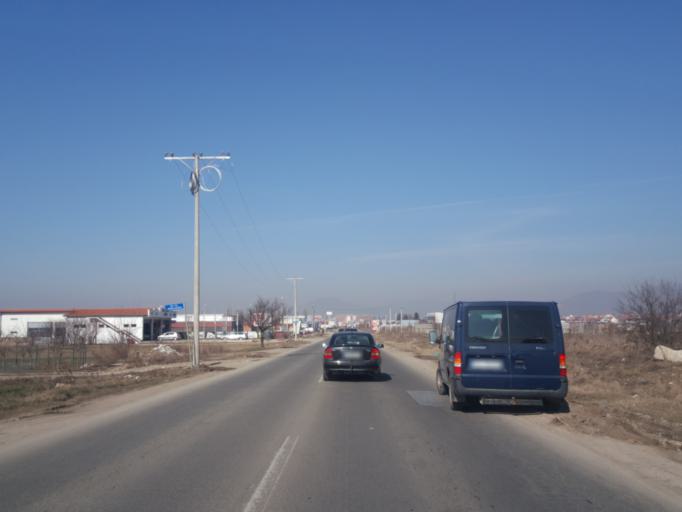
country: XK
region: Mitrovica
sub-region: Vushtrri
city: Vushtrri
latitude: 42.8049
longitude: 20.9914
